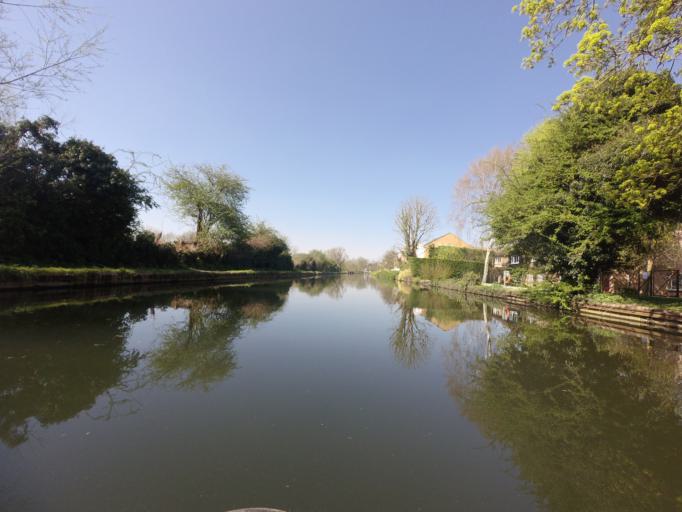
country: GB
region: England
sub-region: Hertfordshire
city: Kings Langley
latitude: 51.7100
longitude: -0.4426
